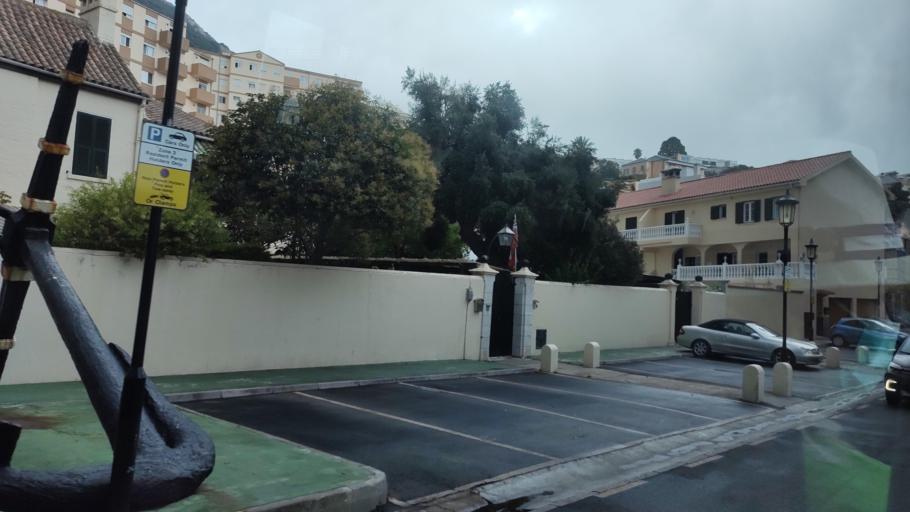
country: GI
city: Gibraltar
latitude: 36.1222
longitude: -5.3519
